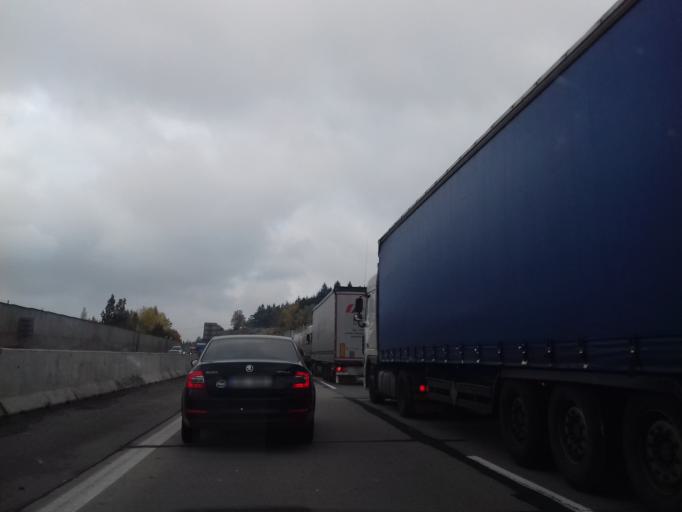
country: CZ
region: Vysocina
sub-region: Okres Zd'ar nad Sazavou
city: Velke Mezirici
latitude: 49.3622
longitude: 16.0093
